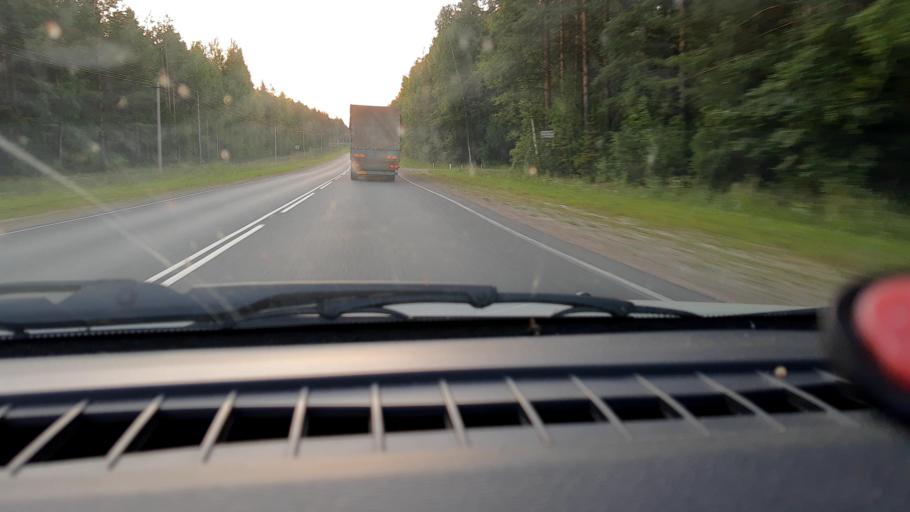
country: RU
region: Nizjnij Novgorod
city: Uren'
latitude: 57.3498
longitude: 45.7054
